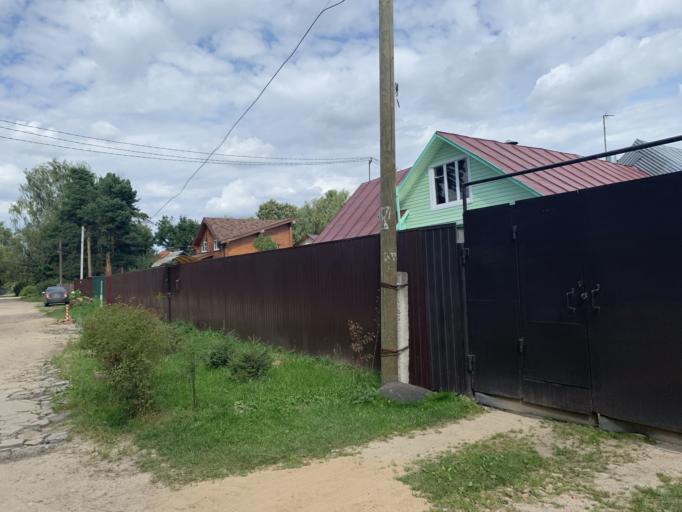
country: RU
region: Moskovskaya
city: Mamontovka
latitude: 55.9861
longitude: 37.8033
